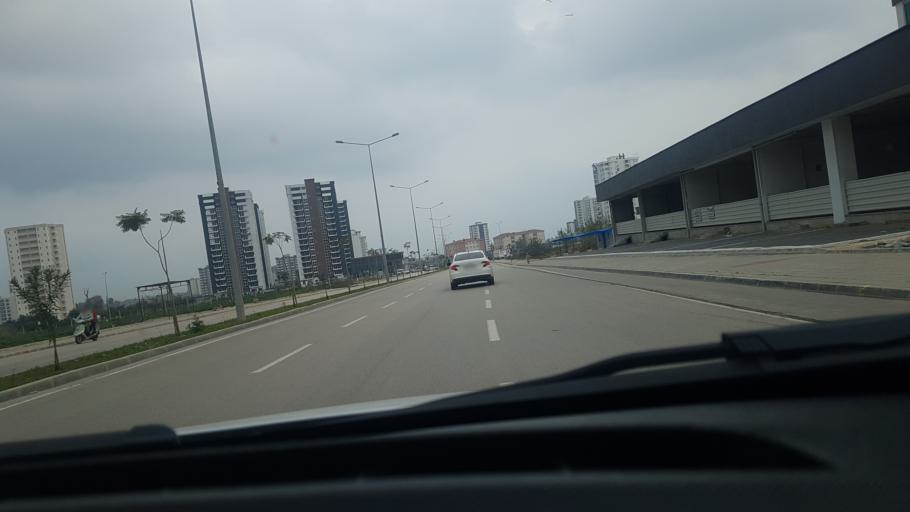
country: TR
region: Adana
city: Seyhan
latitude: 37.0174
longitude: 35.2580
